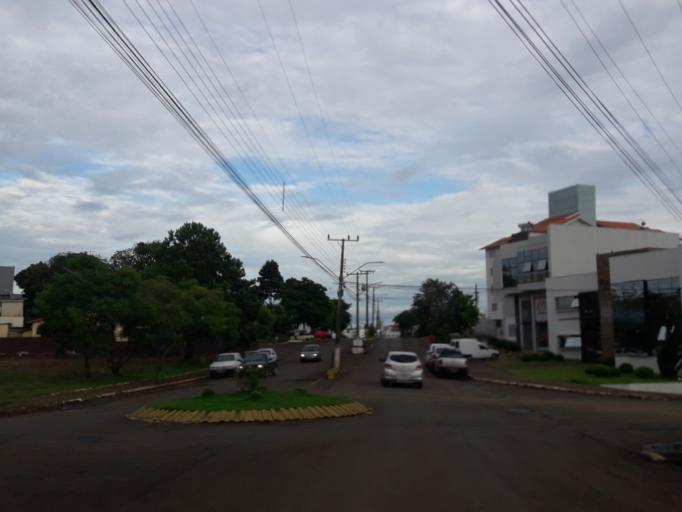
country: AR
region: Misiones
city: Bernardo de Irigoyen
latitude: -26.2597
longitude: -53.6327
